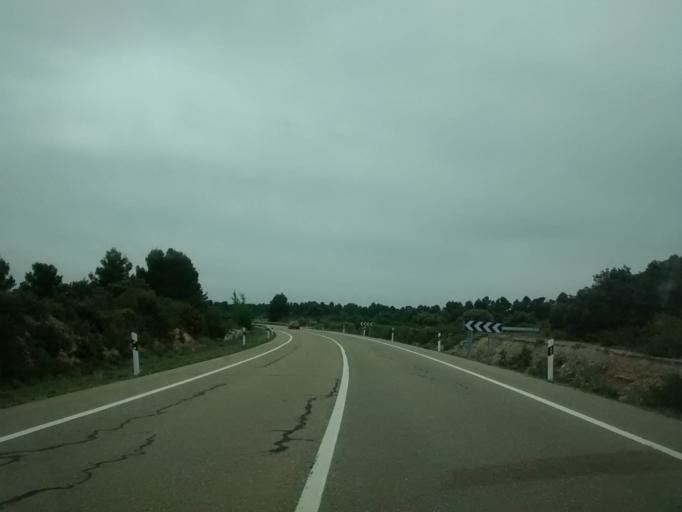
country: ES
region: Aragon
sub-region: Provincia de Teruel
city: Valdealgorfa
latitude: 40.9552
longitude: -0.0152
